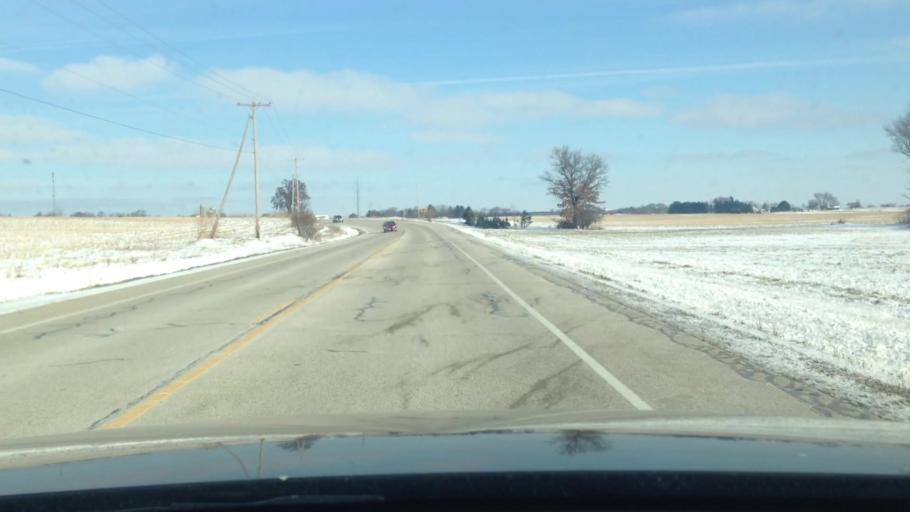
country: US
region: Wisconsin
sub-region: Walworth County
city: Lake Geneva
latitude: 42.6808
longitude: -88.4057
